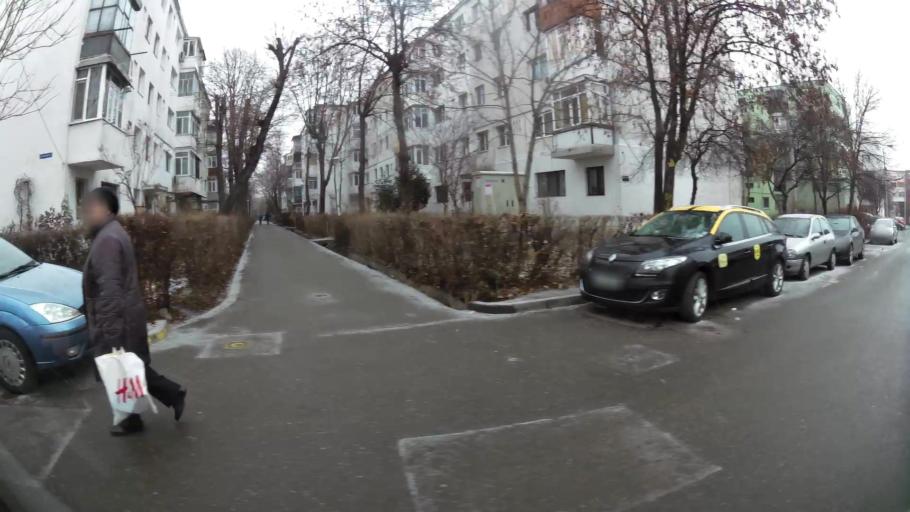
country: RO
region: Prahova
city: Ploiesti
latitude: 44.9394
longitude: 26.0443
